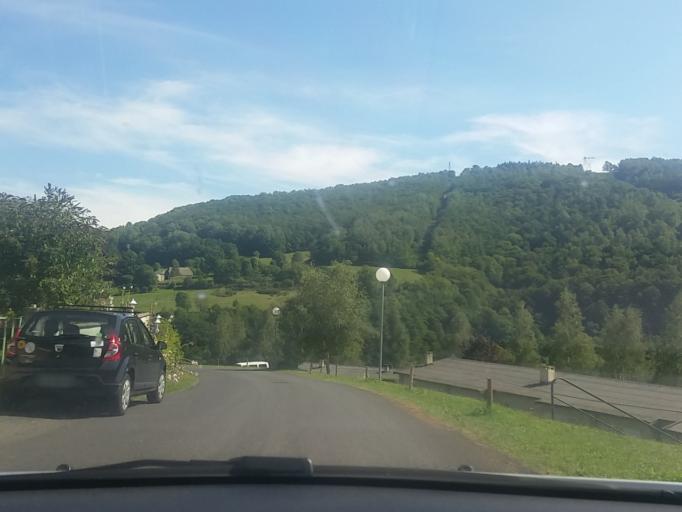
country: FR
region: Auvergne
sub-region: Departement du Cantal
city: Neuveglise
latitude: 44.8948
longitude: 3.0024
